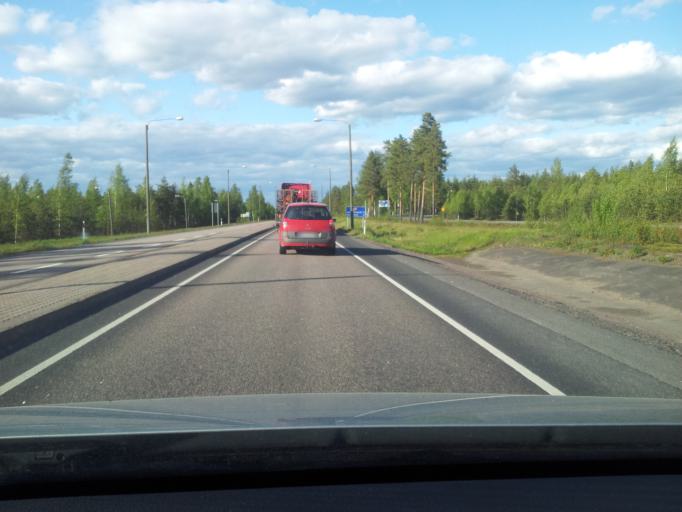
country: FI
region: Kymenlaakso
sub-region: Kouvola
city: Kouvola
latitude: 60.8963
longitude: 26.9127
